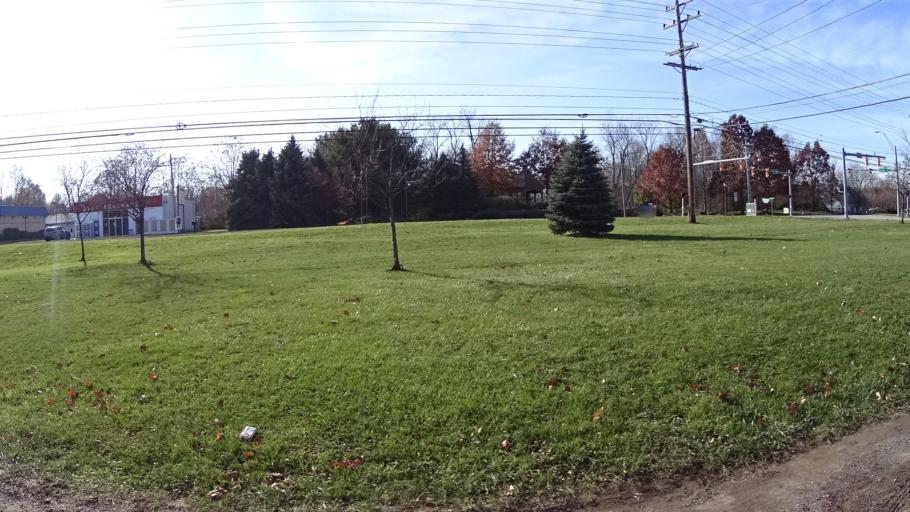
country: US
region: Ohio
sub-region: Lorain County
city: Avon
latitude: 41.4572
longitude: -82.0396
